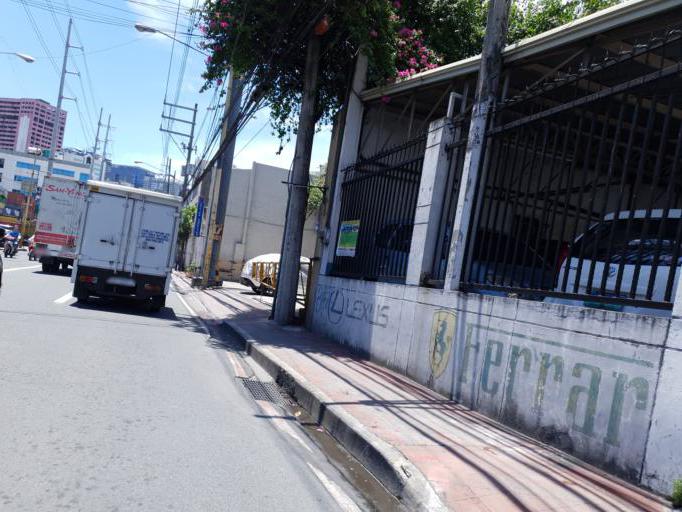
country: PH
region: Metro Manila
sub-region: Makati City
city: Makati City
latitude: 14.5659
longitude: 121.0124
